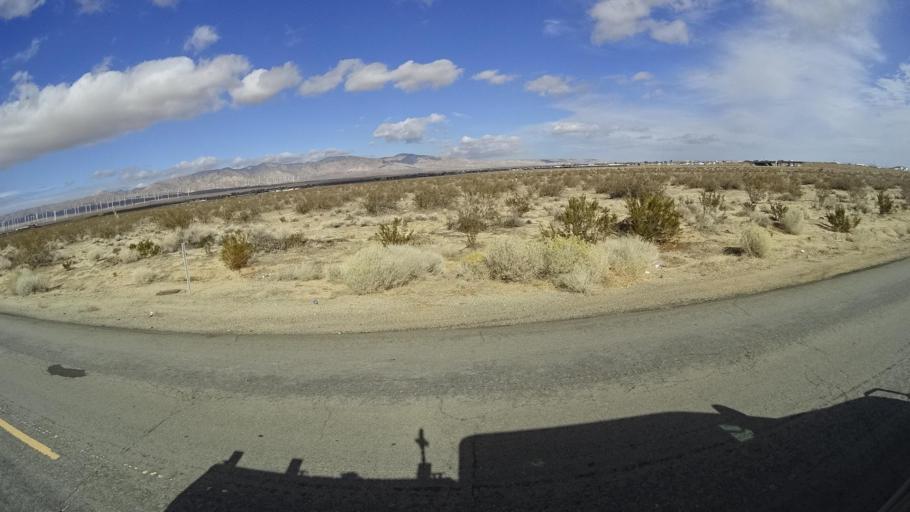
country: US
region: California
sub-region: Kern County
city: Mojave
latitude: 35.0314
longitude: -118.1778
